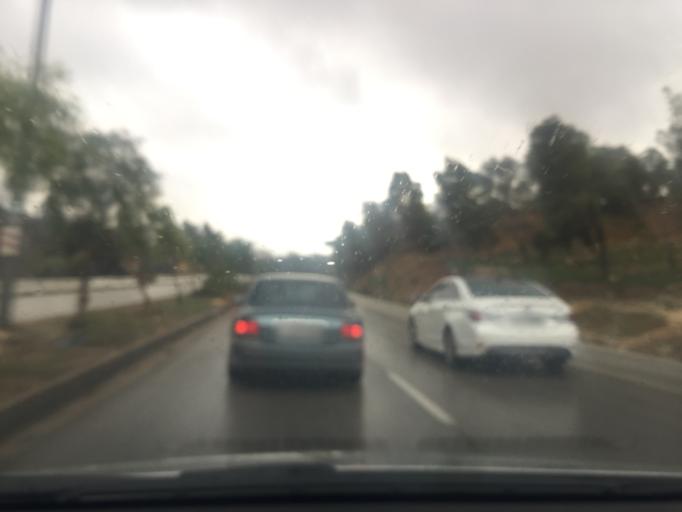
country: JO
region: Amman
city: Amman
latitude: 32.0228
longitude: 35.9506
